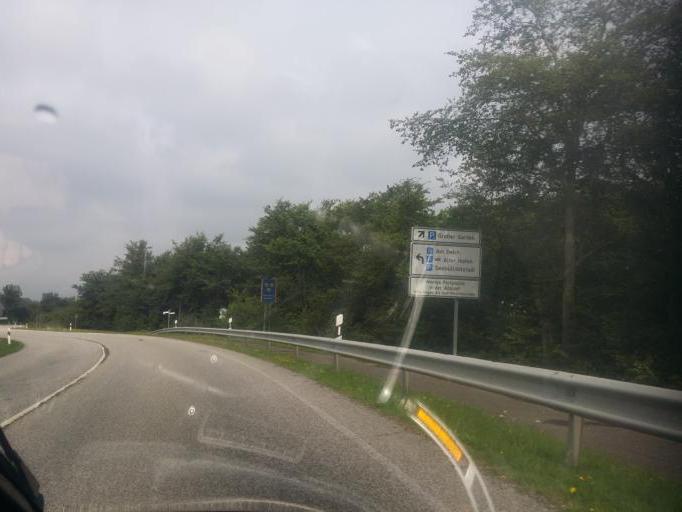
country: DE
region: Schleswig-Holstein
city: Friedrichstadt
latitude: 54.3696
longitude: 9.0965
